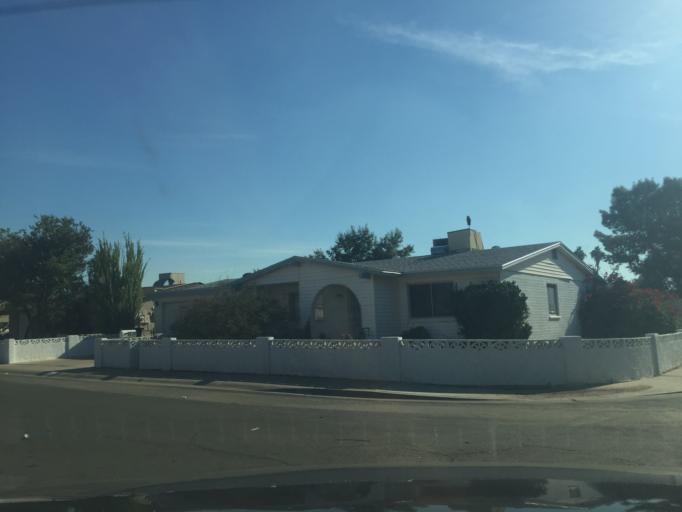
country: US
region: Arizona
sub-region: Maricopa County
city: Tolleson
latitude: 33.4781
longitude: -112.2158
